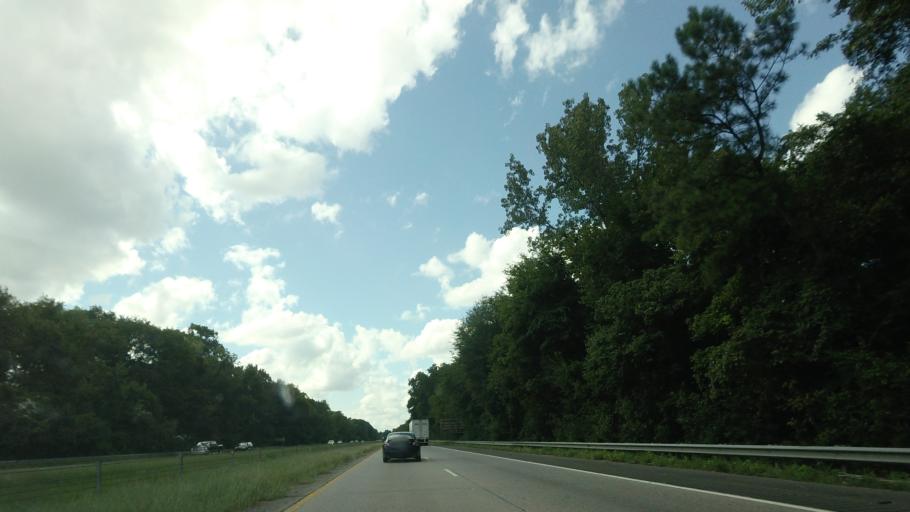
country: US
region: Georgia
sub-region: Bibb County
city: Macon
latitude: 32.8316
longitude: -83.6072
